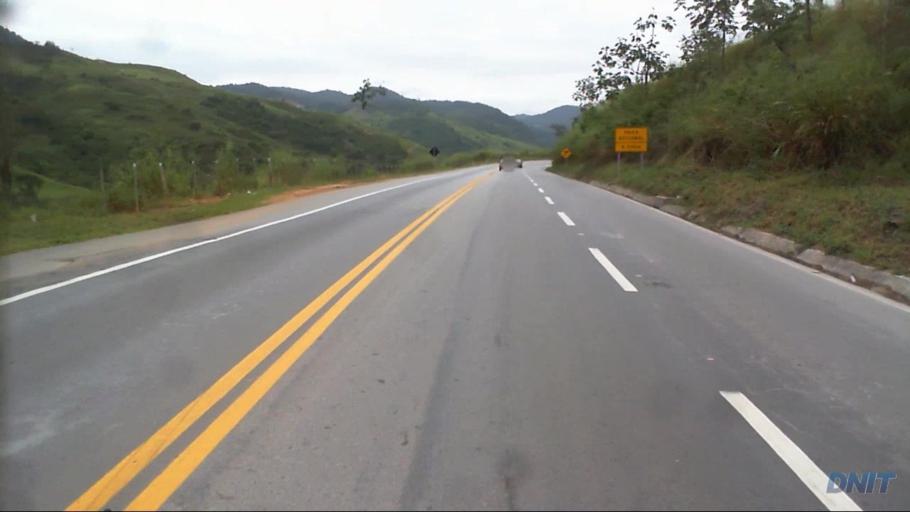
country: BR
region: Minas Gerais
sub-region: Timoteo
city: Timoteo
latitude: -19.6378
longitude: -42.8078
